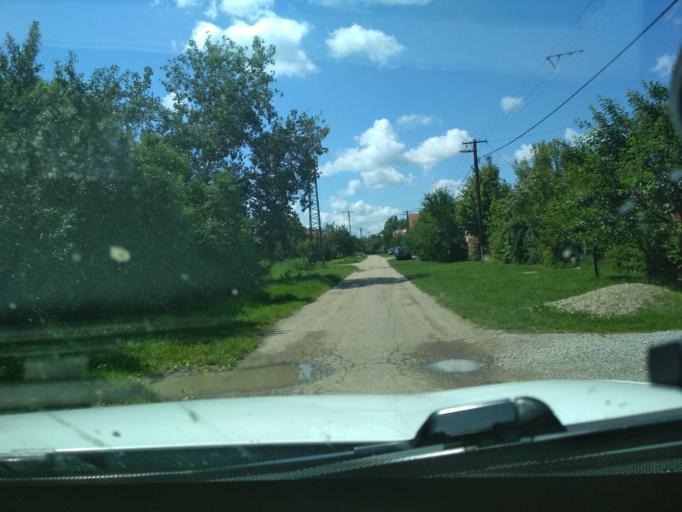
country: HU
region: Jasz-Nagykun-Szolnok
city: Abadszalok
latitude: 47.4831
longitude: 20.6060
